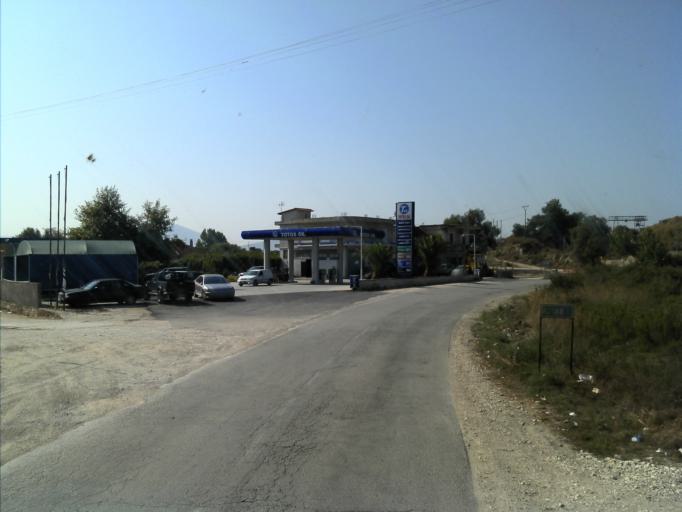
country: AL
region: Vlore
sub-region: Rrethi i Delvines
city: Finiq
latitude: 39.8818
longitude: 20.0560
